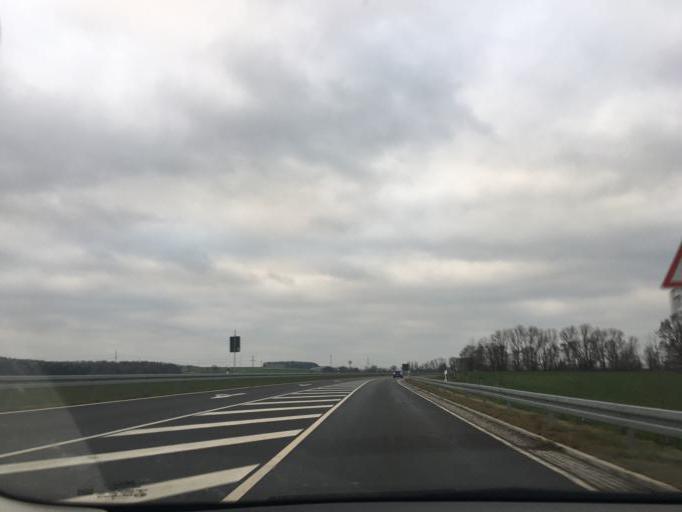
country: DE
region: Saxony
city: Niederfrohna
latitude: 50.8920
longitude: 12.7167
